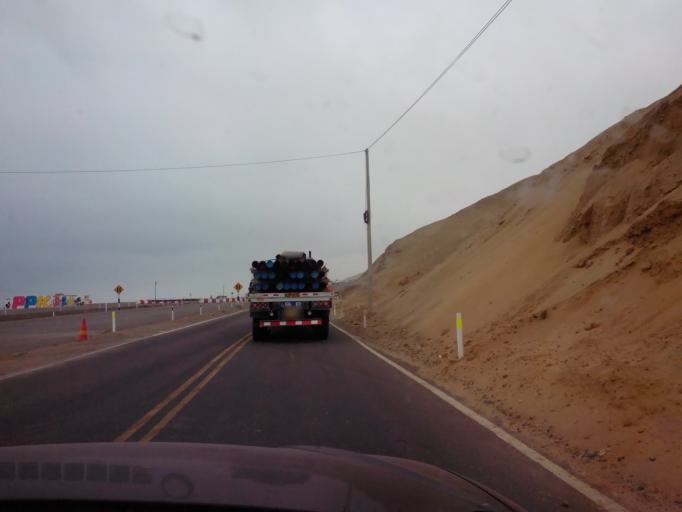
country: PE
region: Ica
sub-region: Provincia de Chincha
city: San Pedro
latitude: -13.3255
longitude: -76.2418
